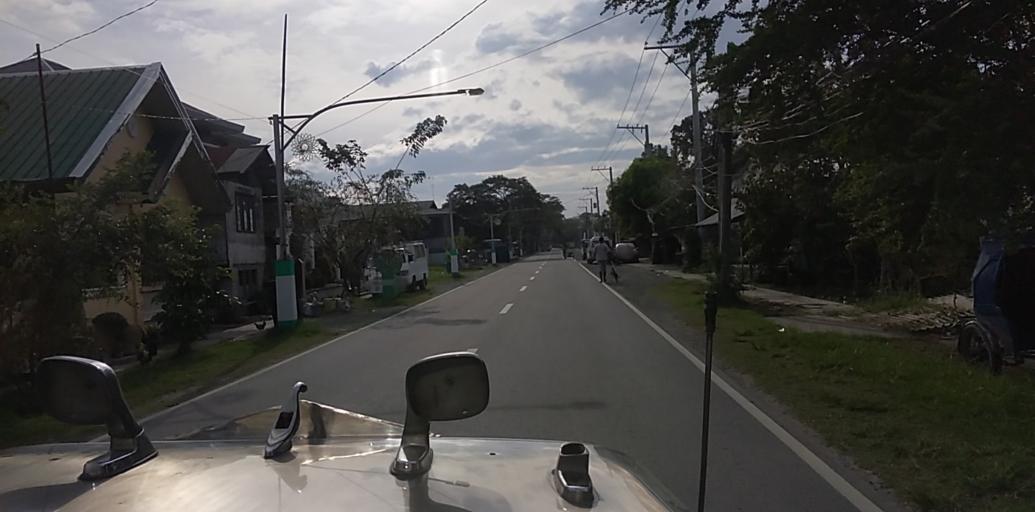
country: PH
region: Central Luzon
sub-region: Province of Pampanga
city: Minalin
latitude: 14.9777
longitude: 120.6883
